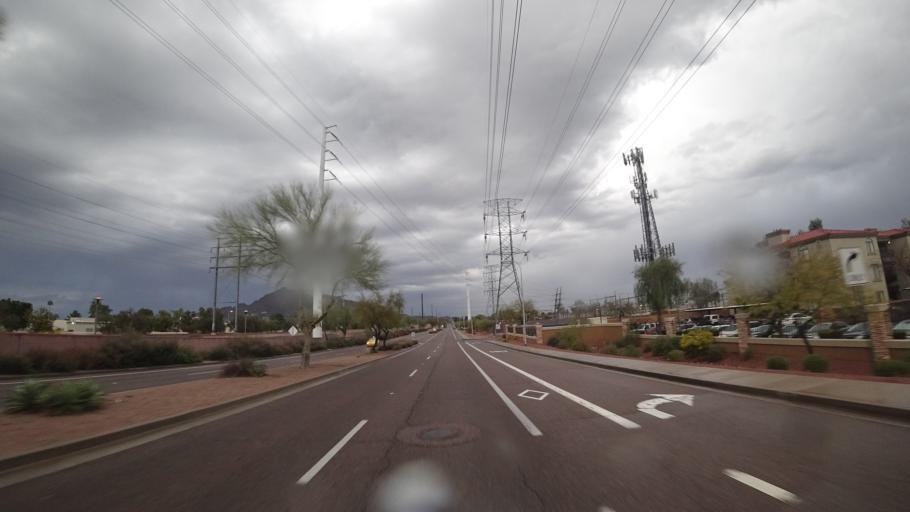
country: US
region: Arizona
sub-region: Maricopa County
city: Paradise Valley
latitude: 33.4816
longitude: -111.9428
